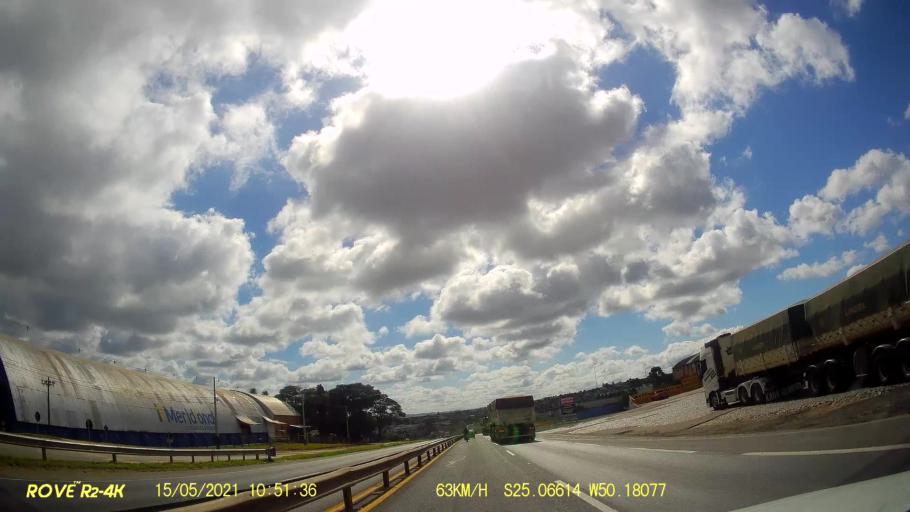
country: BR
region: Parana
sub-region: Ponta Grossa
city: Ponta Grossa
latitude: -25.0662
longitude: -50.1811
